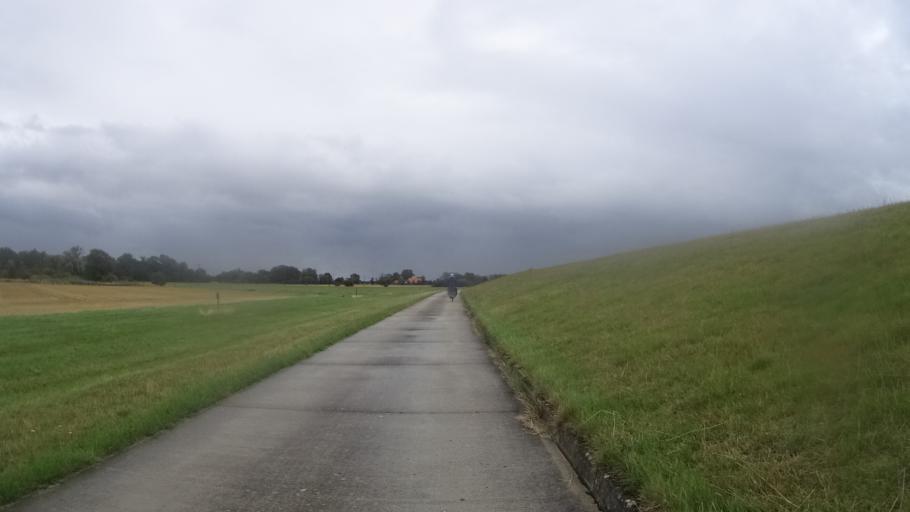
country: DE
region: Lower Saxony
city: Neu Darchau
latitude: 53.2582
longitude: 10.8465
